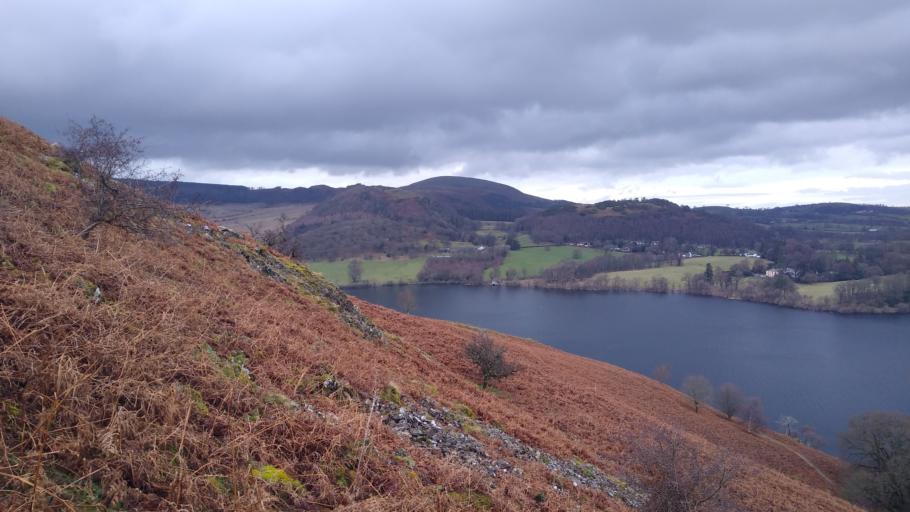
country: GB
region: England
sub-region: Cumbria
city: Penrith
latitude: 54.5734
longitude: -2.8725
